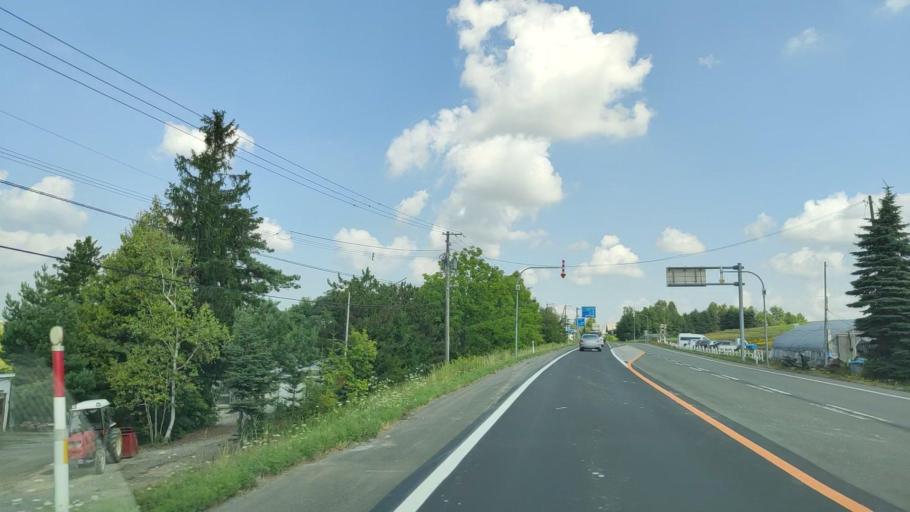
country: JP
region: Hokkaido
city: Shimo-furano
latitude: 43.5416
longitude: 142.4386
